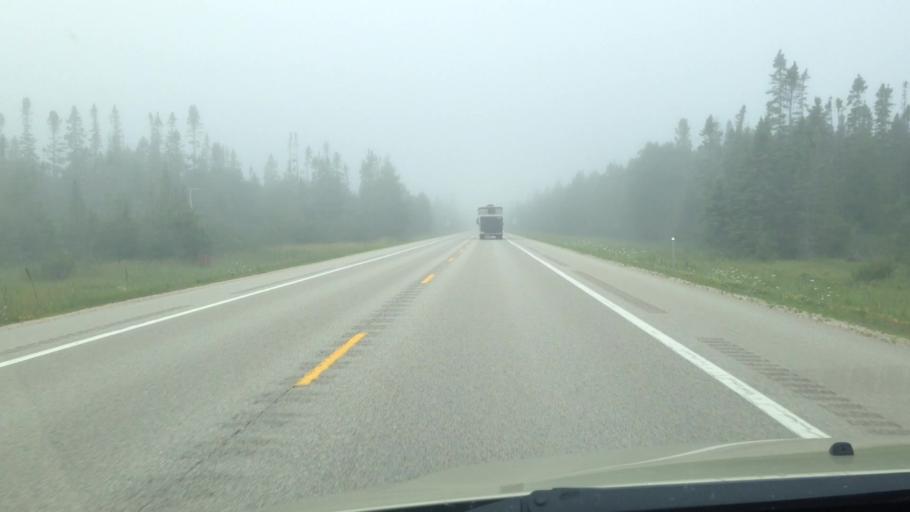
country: US
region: Michigan
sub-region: Luce County
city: Newberry
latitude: 46.1007
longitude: -85.5311
